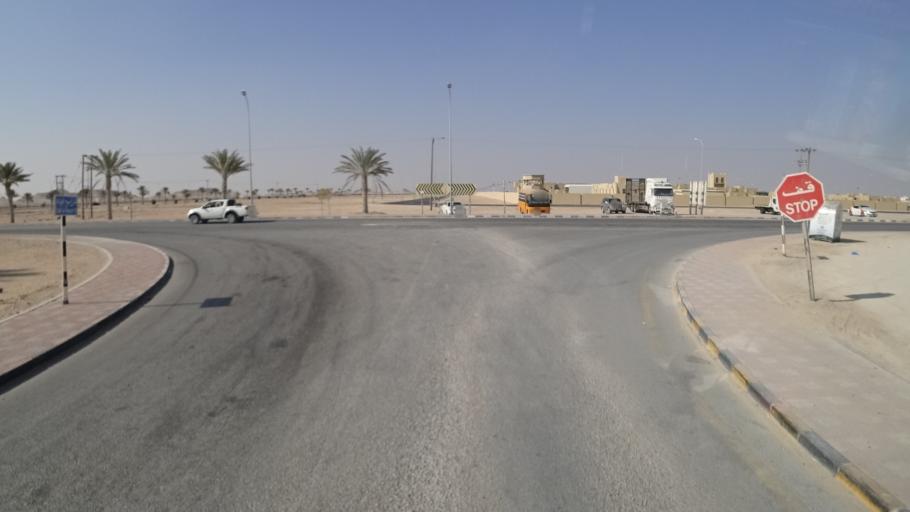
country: OM
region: Zufar
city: Salalah
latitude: 17.6126
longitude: 54.0342
